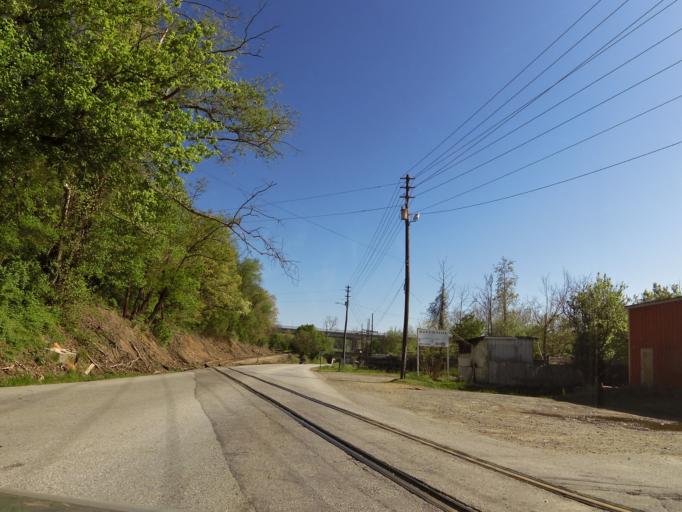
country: US
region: North Carolina
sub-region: Buncombe County
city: Asheville
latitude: 35.5950
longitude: -82.5721
